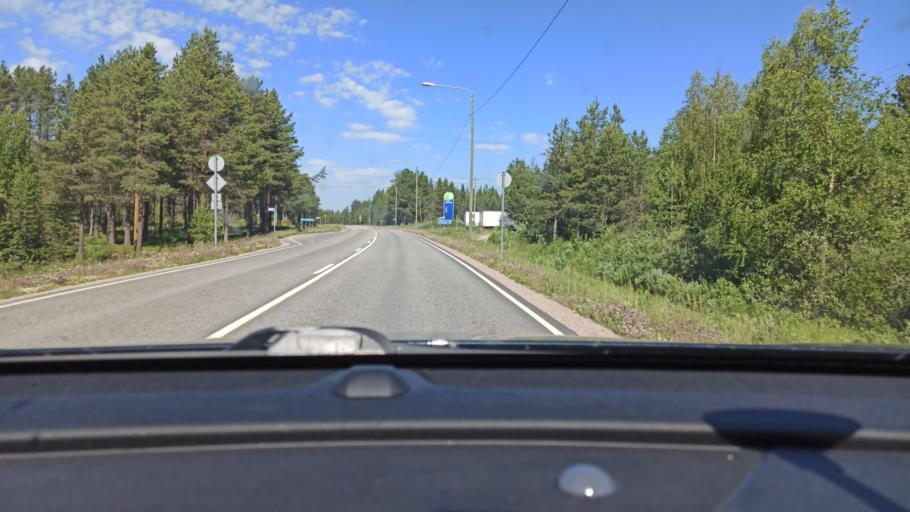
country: FI
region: Lapland
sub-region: Tunturi-Lappi
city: Muonio
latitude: 67.9718
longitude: 23.6796
